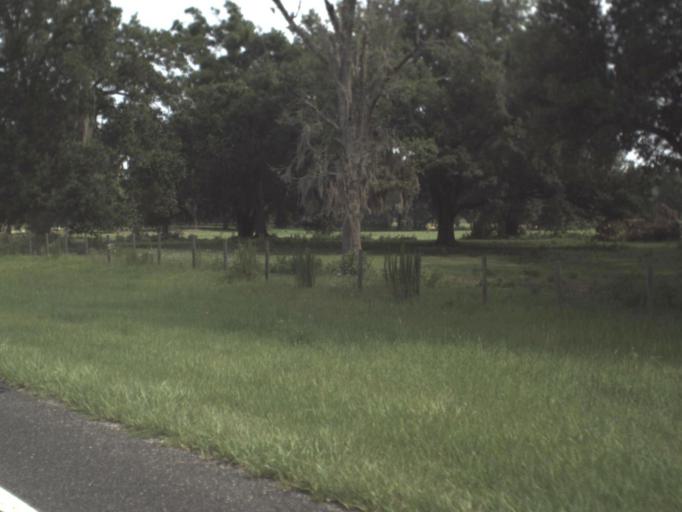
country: US
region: Florida
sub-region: Levy County
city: Williston
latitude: 29.3606
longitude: -82.4047
